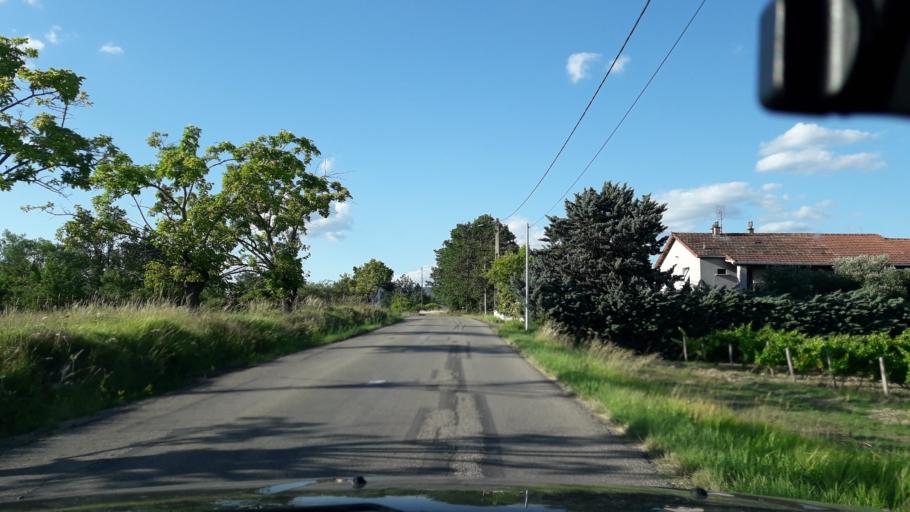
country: FR
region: Rhone-Alpes
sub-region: Departement de l'Ardeche
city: Lavilledieu
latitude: 44.5920
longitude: 4.4595
